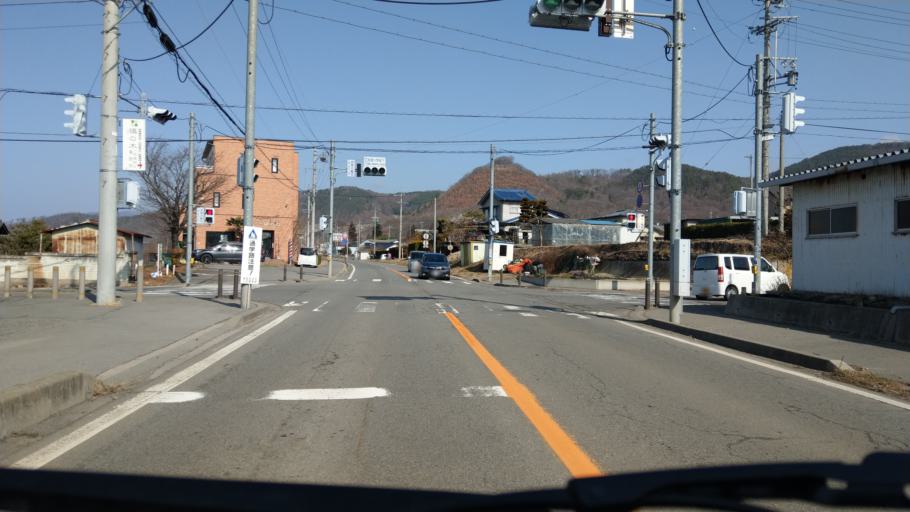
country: JP
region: Nagano
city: Ueda
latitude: 36.3692
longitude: 138.3515
